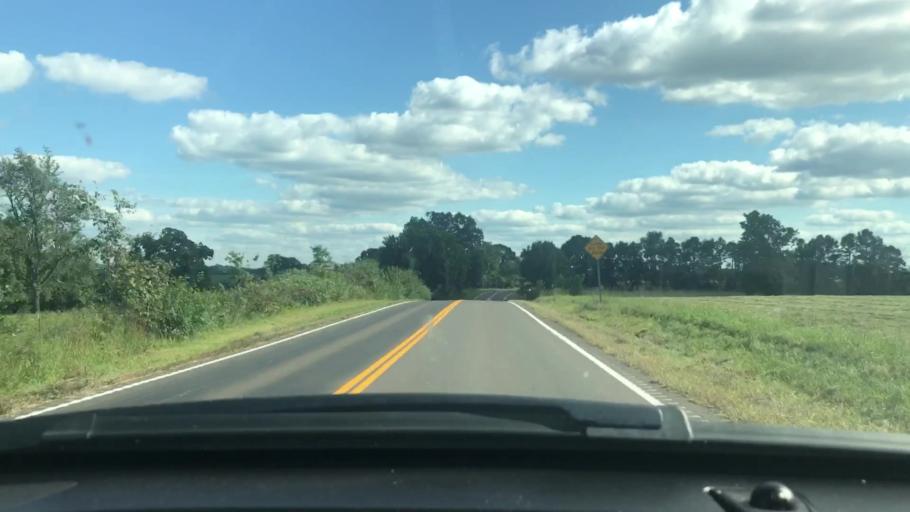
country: US
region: Missouri
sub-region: Wright County
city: Mountain Grove
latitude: 37.1786
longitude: -92.2681
